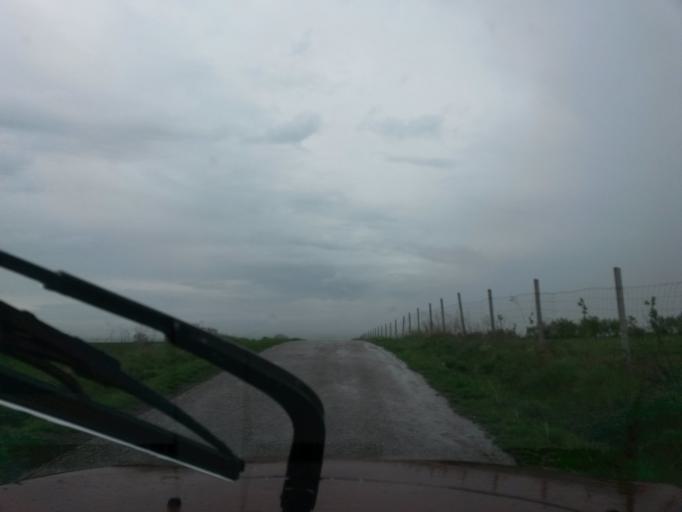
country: HU
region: Borsod-Abauj-Zemplen
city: Gonc
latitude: 48.5152
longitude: 21.3232
